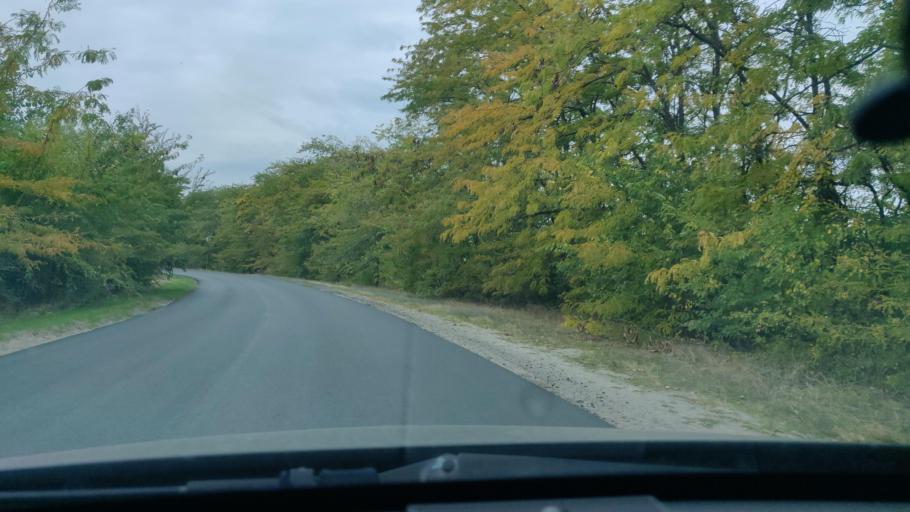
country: RU
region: Rostov
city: Ust'-Donetskiy
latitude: 47.6477
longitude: 40.8788
